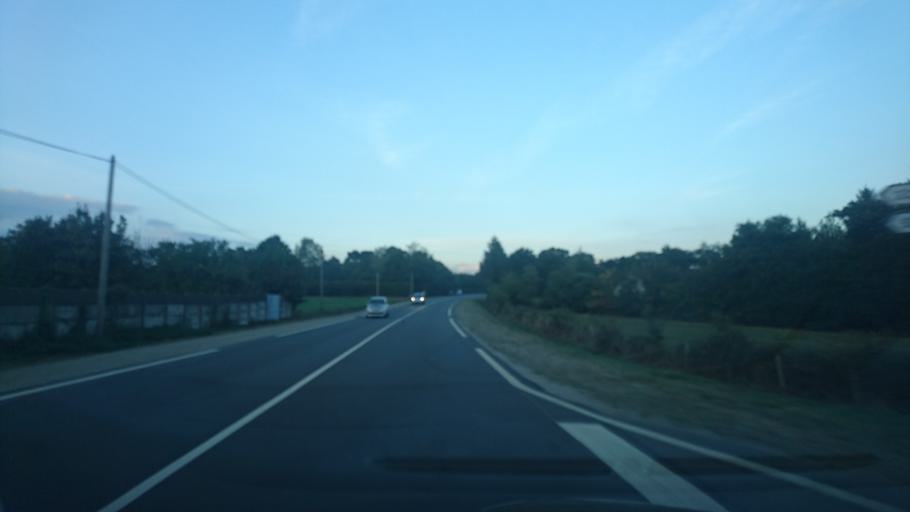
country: FR
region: Brittany
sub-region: Departement d'Ille-et-Vilaine
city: Lassy
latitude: 47.9731
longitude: -1.8481
